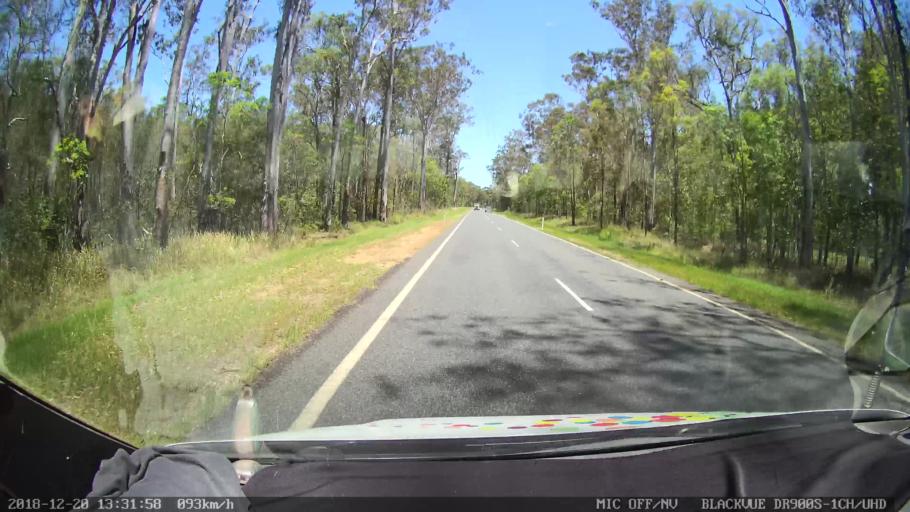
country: AU
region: New South Wales
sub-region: Clarence Valley
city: Gordon
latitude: -29.2255
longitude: 152.9881
